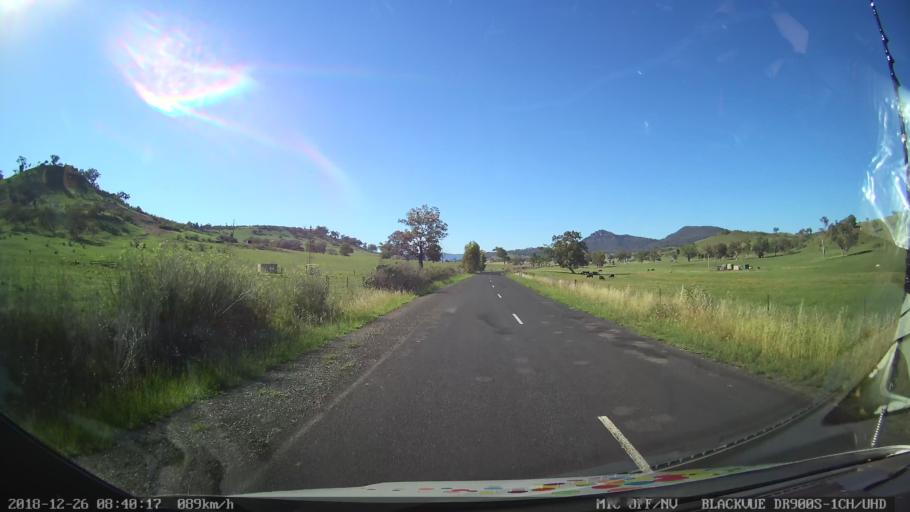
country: AU
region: New South Wales
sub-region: Mid-Western Regional
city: Kandos
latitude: -32.4649
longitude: 150.0762
